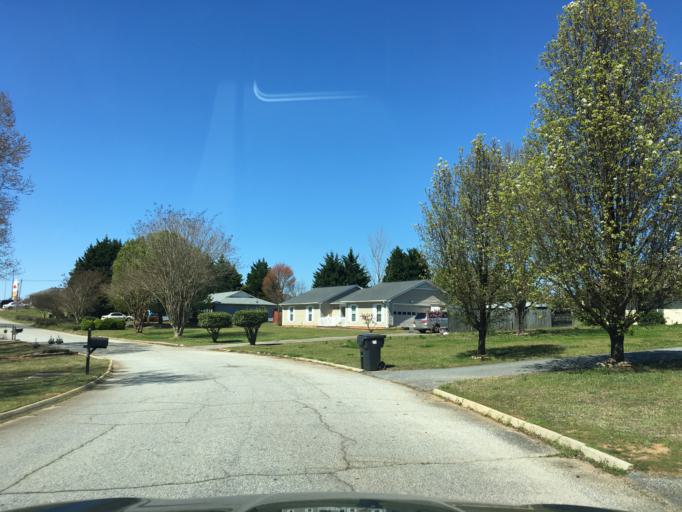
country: US
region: South Carolina
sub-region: Spartanburg County
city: Wellford
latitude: 34.8845
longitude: -82.0670
